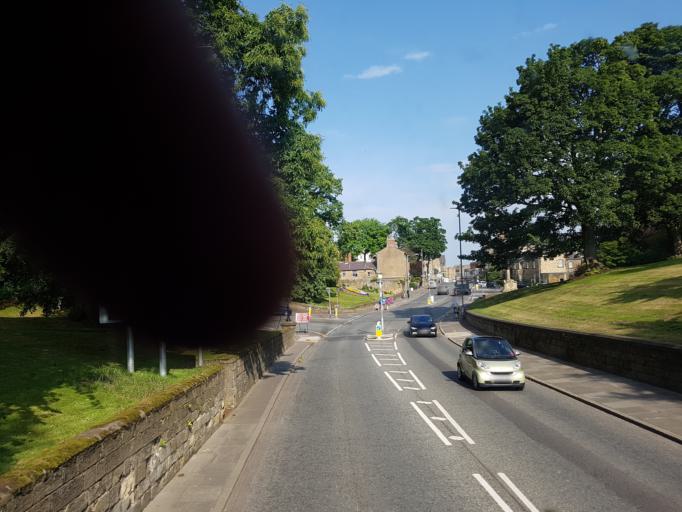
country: GB
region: England
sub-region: Northumberland
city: Alnwick
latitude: 55.4106
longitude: -1.6995
